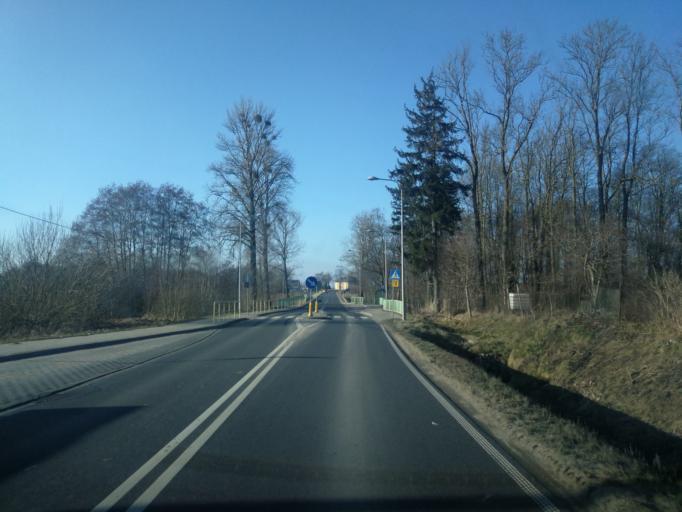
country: PL
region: Warmian-Masurian Voivodeship
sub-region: Powiat ilawski
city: Lubawa
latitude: 53.4250
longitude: 19.7773
